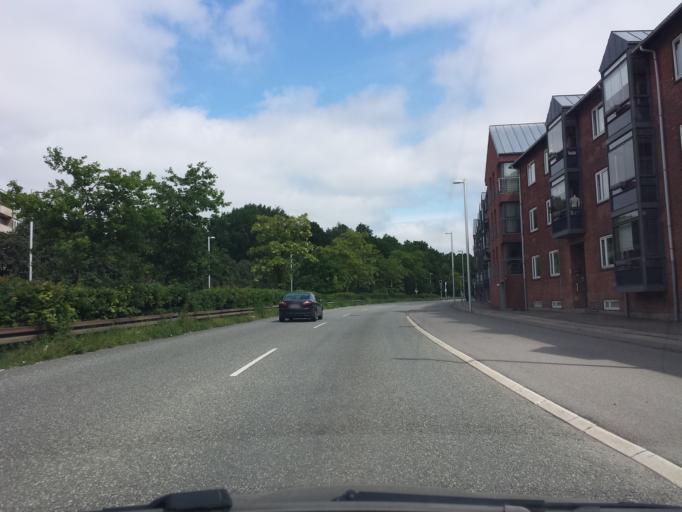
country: DK
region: Capital Region
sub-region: Glostrup Kommune
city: Glostrup
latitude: 55.6669
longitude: 12.3889
